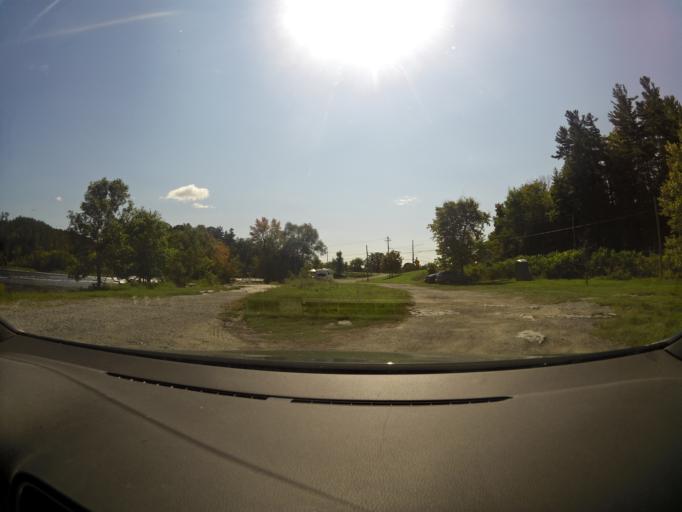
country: CA
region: Ontario
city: Arnprior
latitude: 45.3371
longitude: -76.2880
